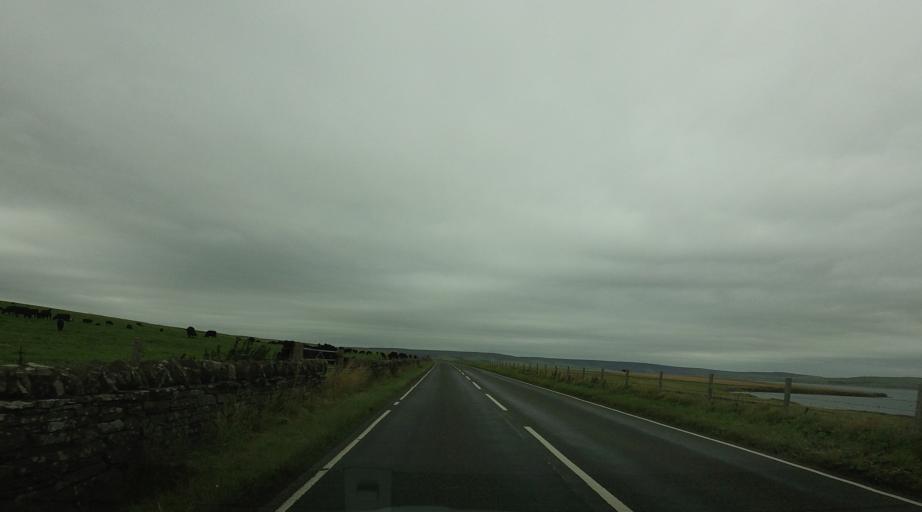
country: GB
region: Scotland
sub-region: Orkney Islands
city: Orkney
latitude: 59.0012
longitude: -2.9966
